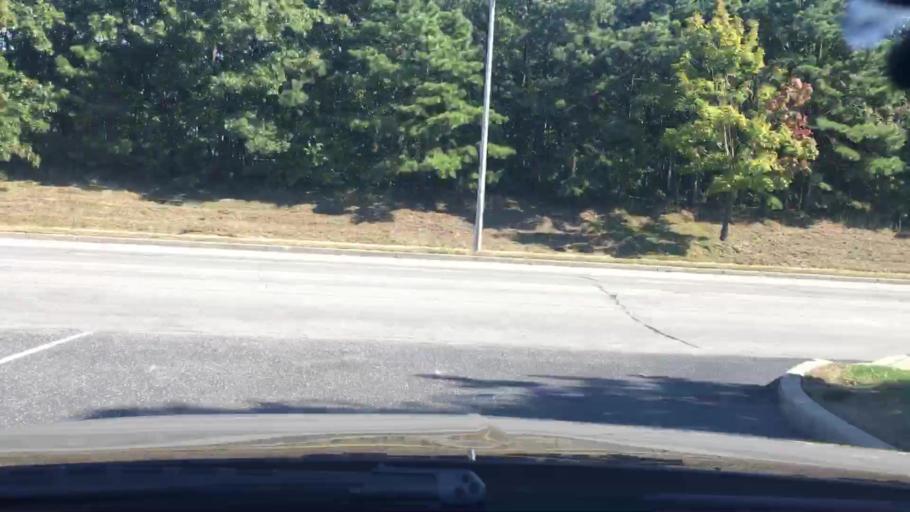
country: US
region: New York
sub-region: Suffolk County
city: Holtsville
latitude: 40.8061
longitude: -73.0381
